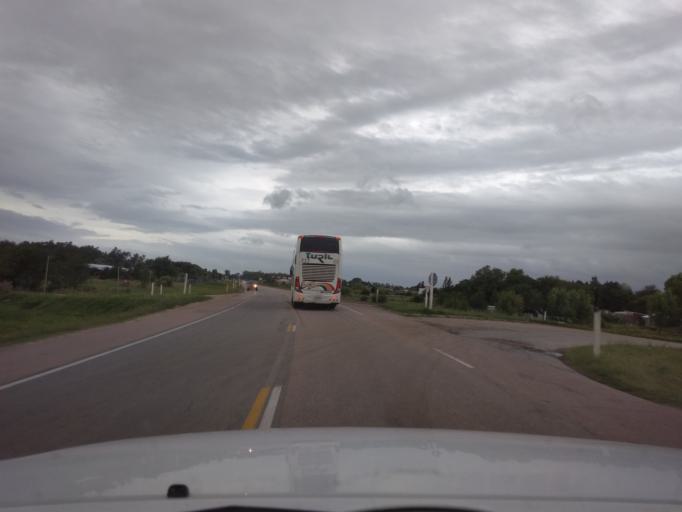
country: UY
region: Canelones
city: Canelones
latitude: -34.5076
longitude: -56.2807
